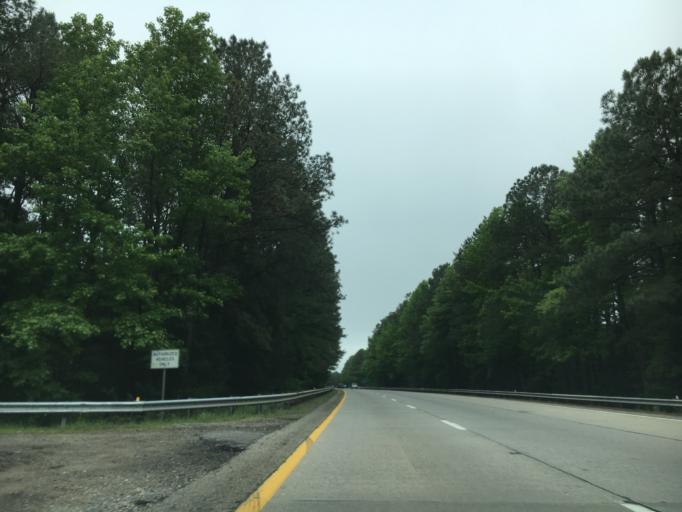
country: US
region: Virginia
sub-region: Chesterfield County
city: Matoaca
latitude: 37.1819
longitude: -77.4929
